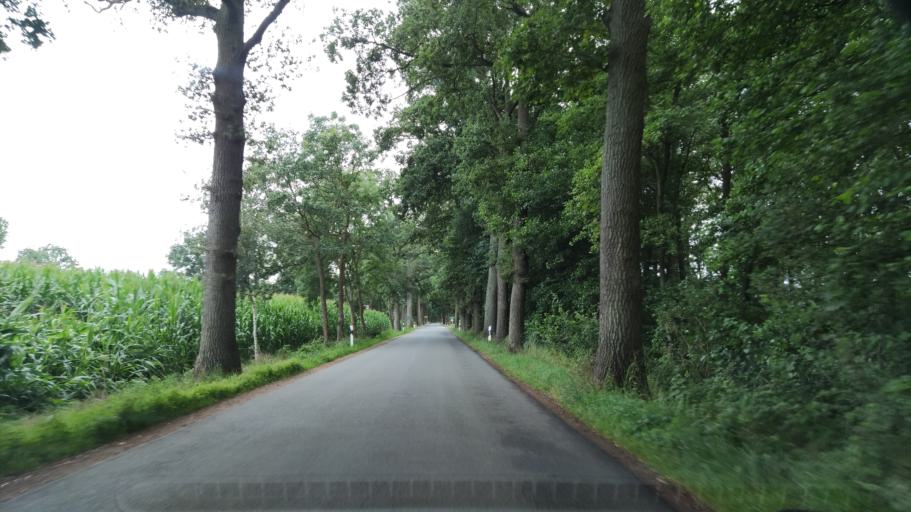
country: DE
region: Lower Saxony
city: Jameln
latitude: 53.0645
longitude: 11.1312
